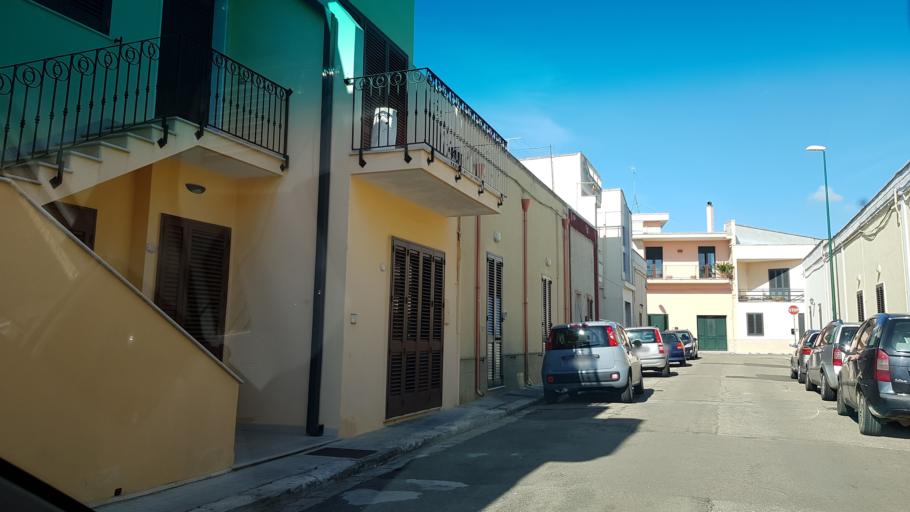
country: IT
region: Apulia
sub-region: Provincia di Lecce
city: Campi Salentina
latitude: 40.3975
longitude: 18.0152
